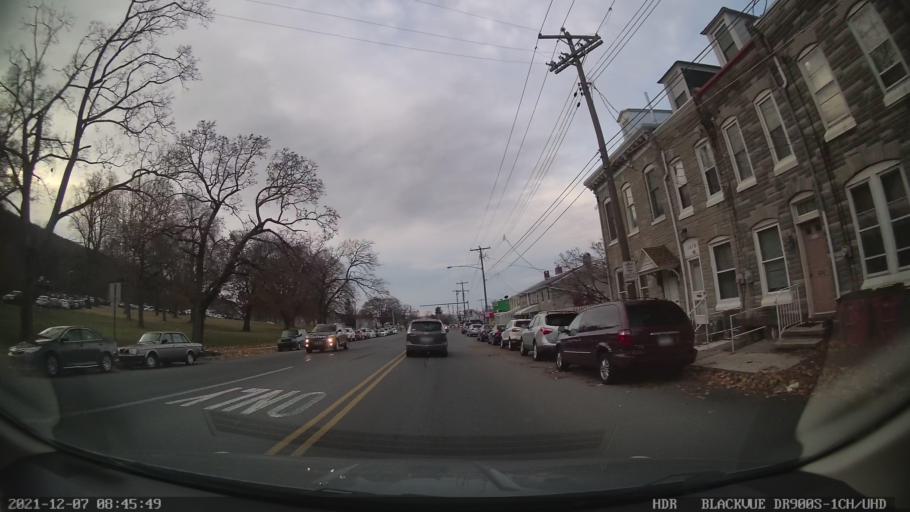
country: US
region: Pennsylvania
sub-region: Berks County
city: Reading
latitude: 40.3515
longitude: -75.9111
